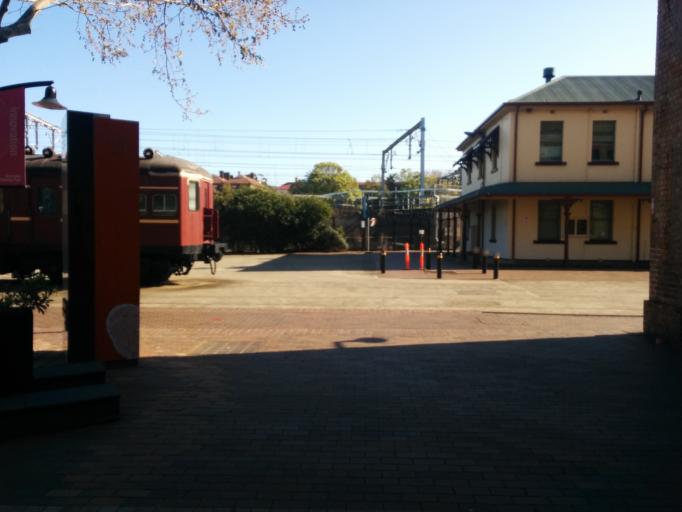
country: AU
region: New South Wales
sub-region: City of Sydney
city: Darlington
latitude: -33.8939
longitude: 151.1968
